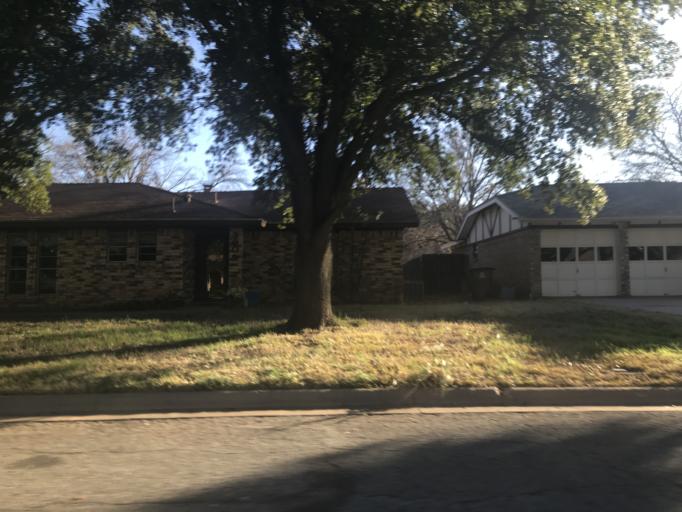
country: US
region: Texas
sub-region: Tom Green County
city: San Angelo
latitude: 31.4302
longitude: -100.4936
